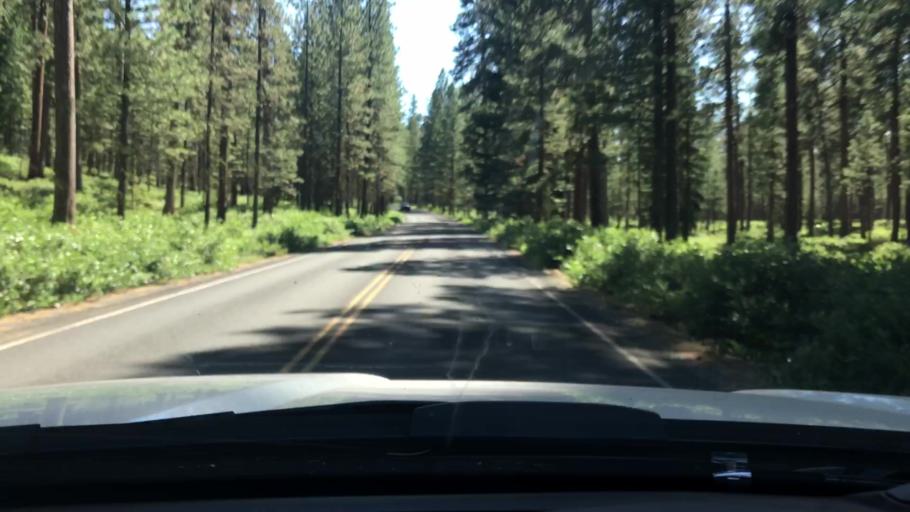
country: US
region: Oregon
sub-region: Deschutes County
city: Sisters
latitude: 44.4128
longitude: -121.6724
